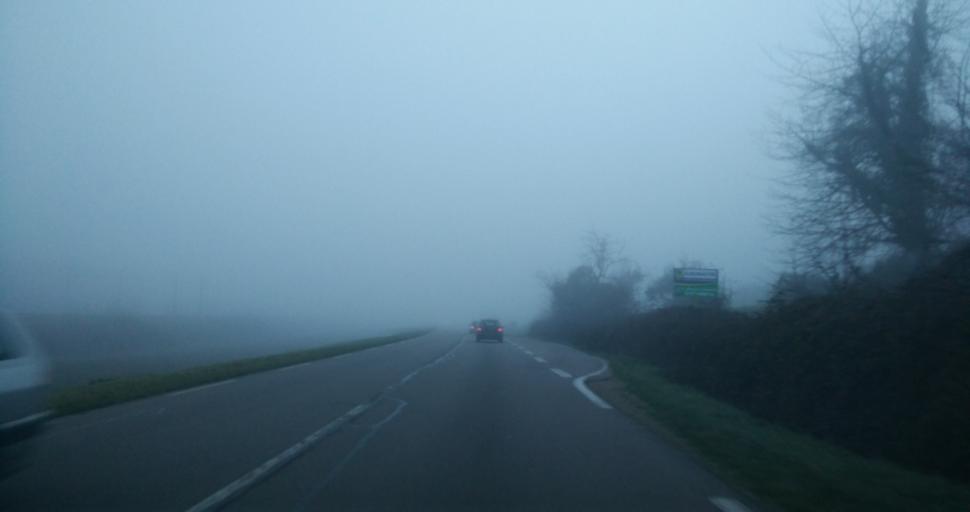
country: FR
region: Haute-Normandie
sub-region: Departement de l'Eure
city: Saint-Just
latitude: 49.1373
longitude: 1.4217
